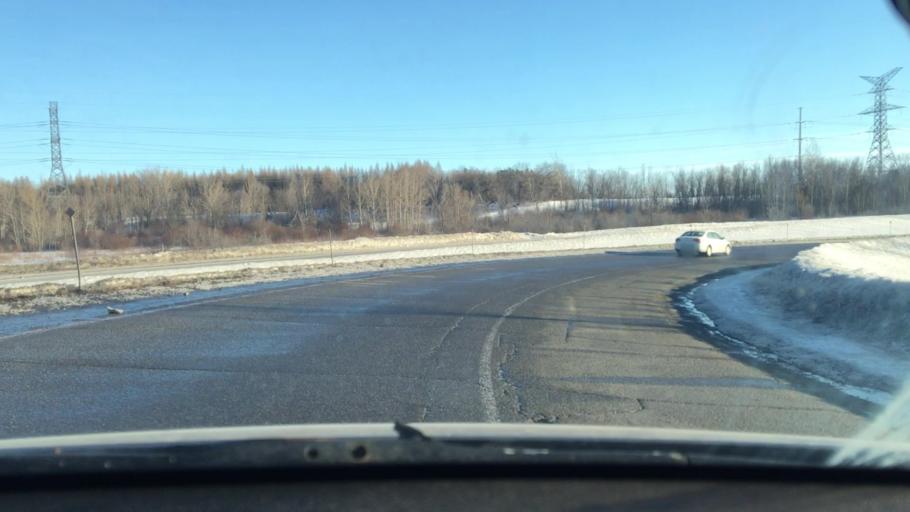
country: CA
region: Ontario
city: Ottawa
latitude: 45.3979
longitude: -75.5906
